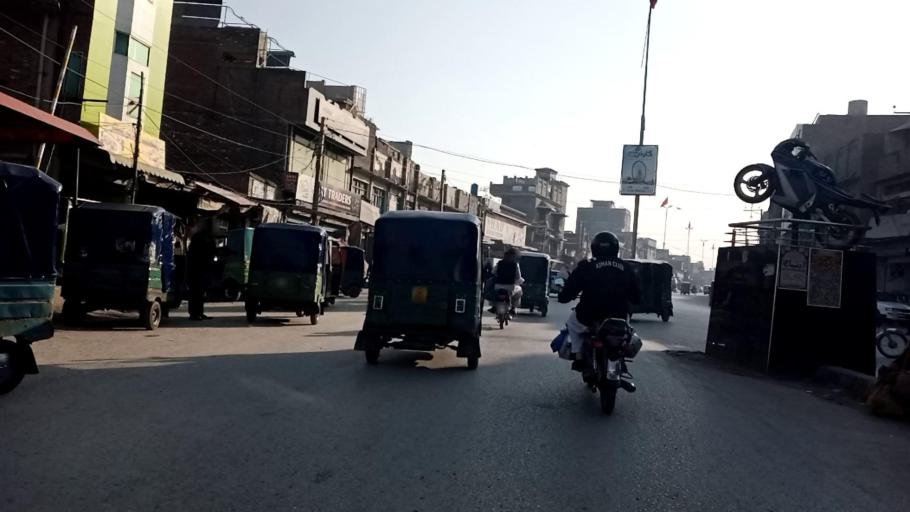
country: PK
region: Khyber Pakhtunkhwa
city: Peshawar
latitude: 34.0024
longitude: 71.5683
